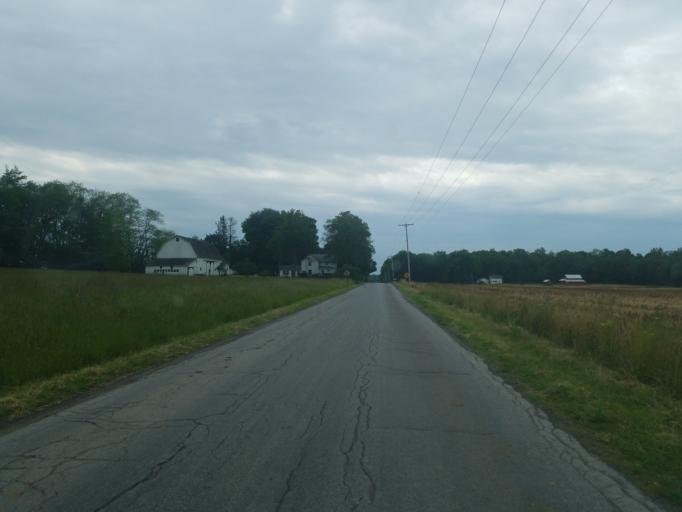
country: US
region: Ohio
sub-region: Richland County
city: Lexington
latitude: 40.5865
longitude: -82.6152
